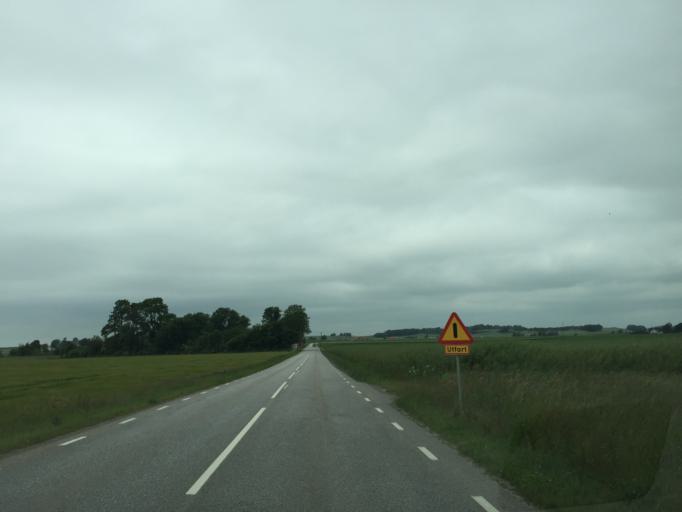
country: SE
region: Skane
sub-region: Ystads Kommun
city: Kopingebro
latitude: 55.4337
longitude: 14.0055
